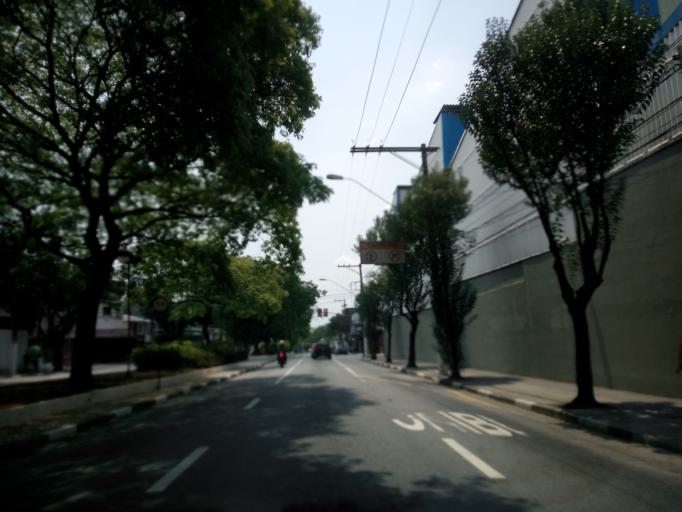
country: BR
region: Sao Paulo
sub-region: Santo Andre
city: Santo Andre
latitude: -23.6626
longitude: -46.5699
